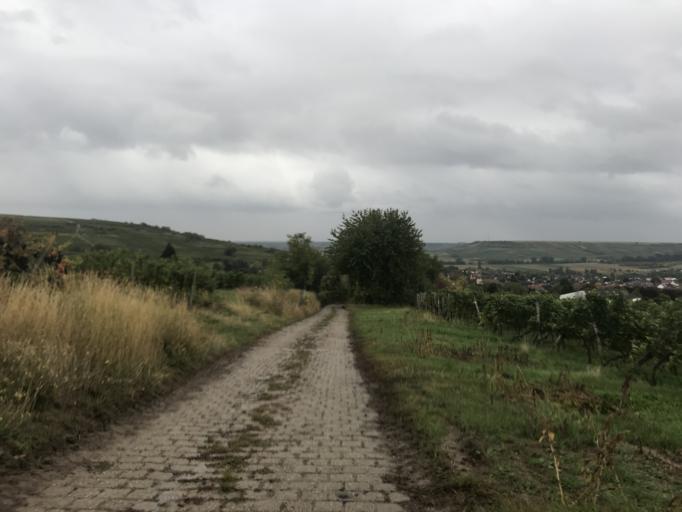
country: DE
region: Rheinland-Pfalz
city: Schwabenheim
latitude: 49.9371
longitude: 8.0976
